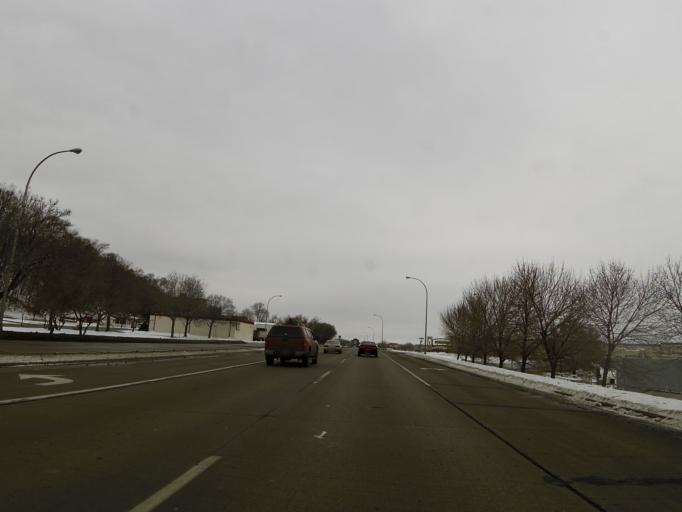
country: US
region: Minnesota
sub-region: Dakota County
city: South Saint Paul
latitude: 44.8864
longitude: -93.0324
